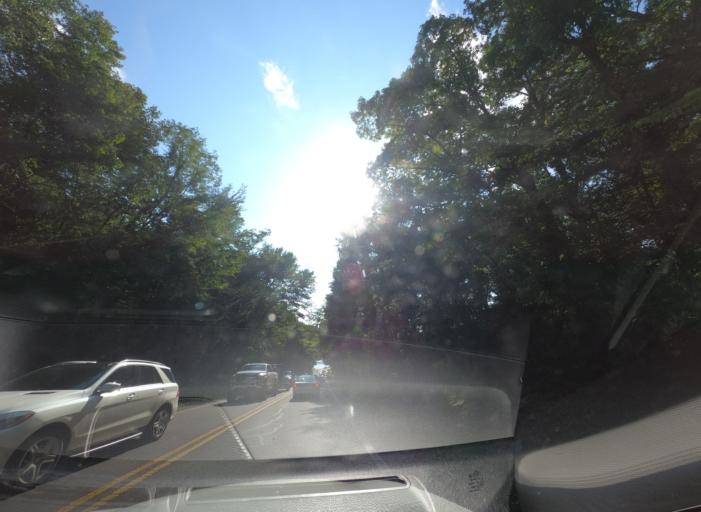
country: US
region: Alabama
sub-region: Jackson County
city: Scottsboro
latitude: 34.6347
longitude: -85.9670
